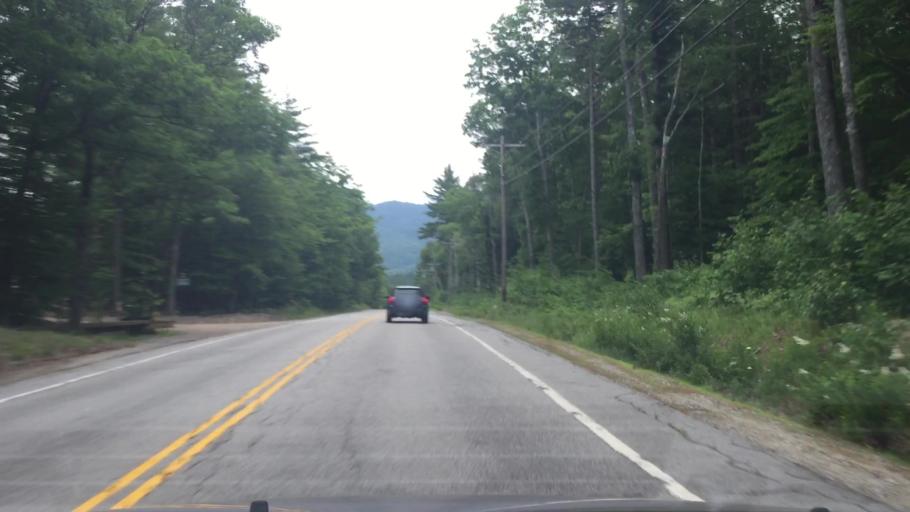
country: US
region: New Hampshire
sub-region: Carroll County
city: North Conway
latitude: 44.0771
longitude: -71.3132
